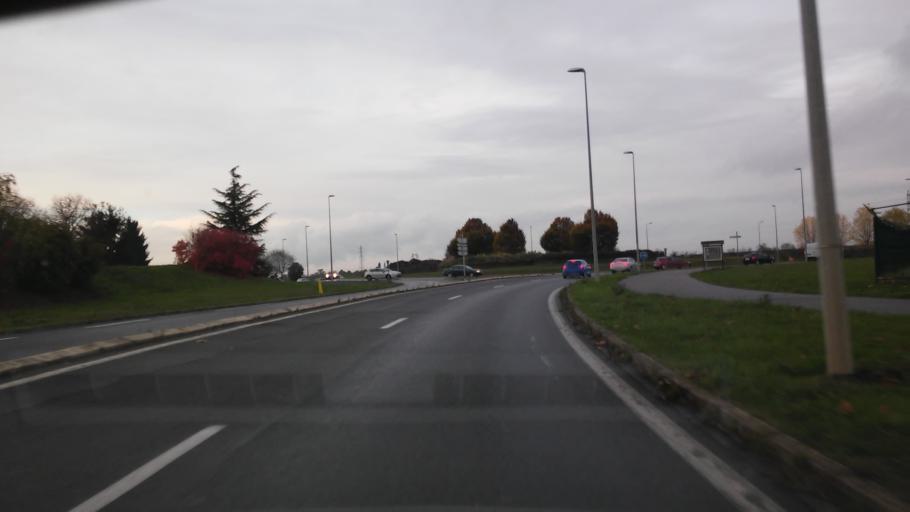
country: FR
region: Lorraine
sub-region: Departement de la Moselle
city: Ay-sur-Moselle
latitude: 49.2434
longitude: 6.2105
